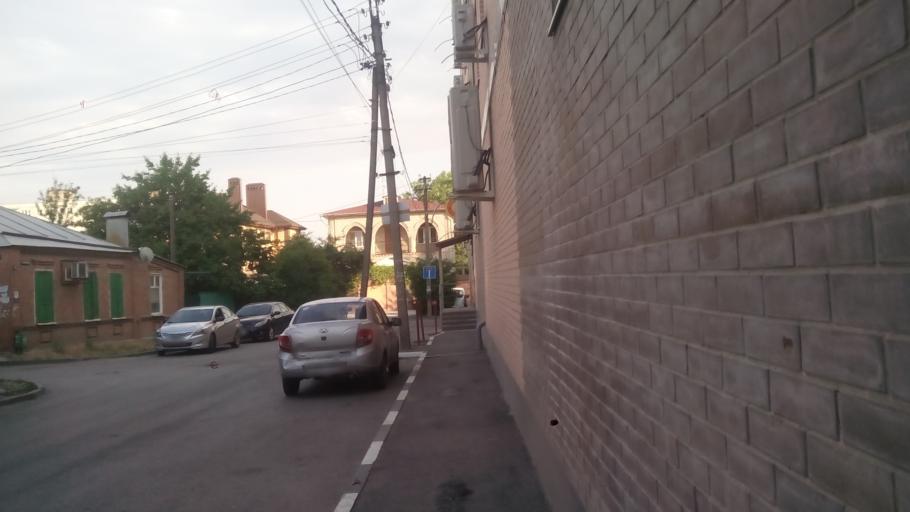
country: RU
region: Rostov
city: Imeni Chkalova
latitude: 47.2490
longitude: 39.7521
